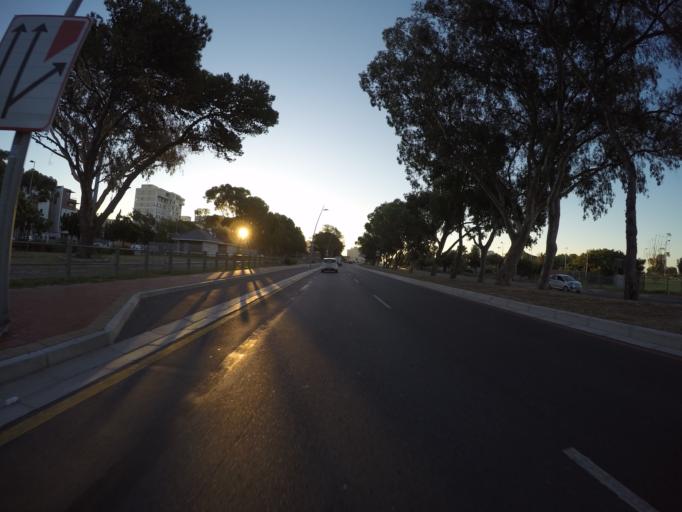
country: ZA
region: Western Cape
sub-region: City of Cape Town
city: Cape Town
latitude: -33.9072
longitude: 18.4052
